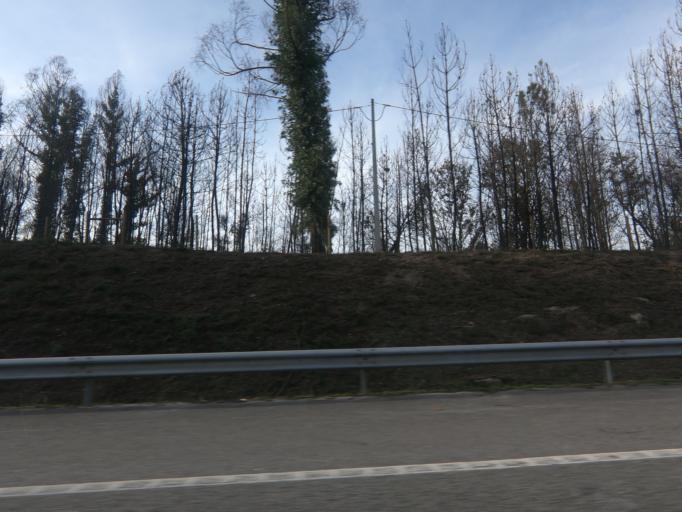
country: PT
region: Viseu
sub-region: Santa Comba Dao
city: Santa Comba Dao
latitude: 40.4325
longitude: -8.1128
